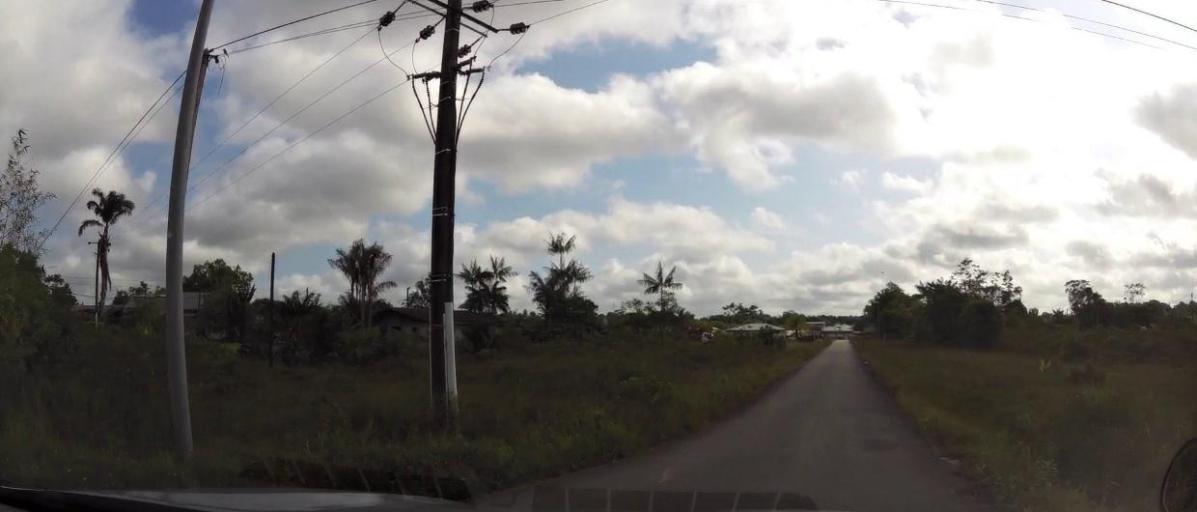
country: GF
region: Guyane
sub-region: Guyane
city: Matoury
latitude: 4.7931
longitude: -52.3566
